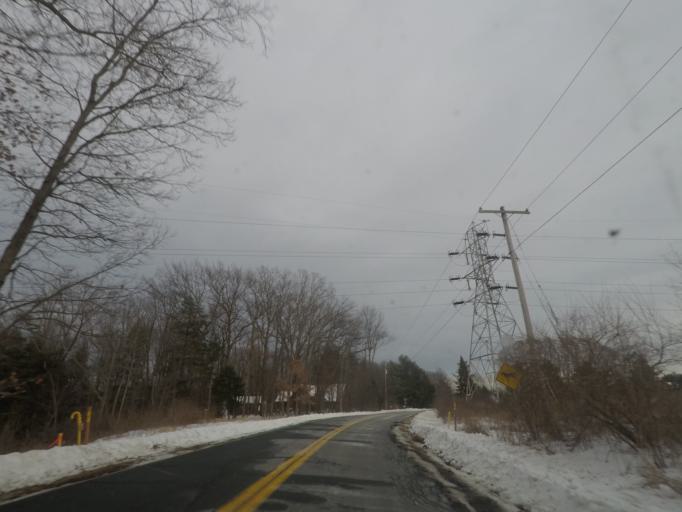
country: US
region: New York
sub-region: Rensselaer County
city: Castleton-on-Hudson
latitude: 42.5164
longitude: -73.7315
